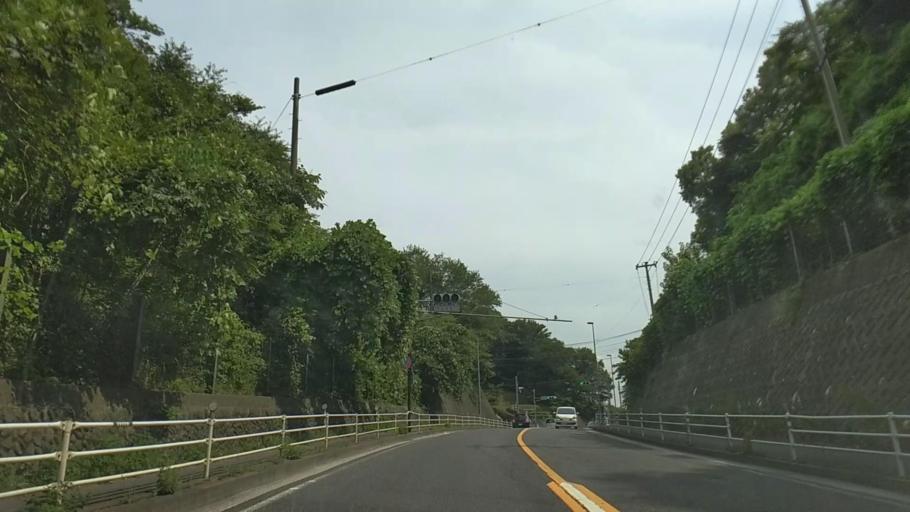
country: JP
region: Tokyo
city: Hachioji
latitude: 35.6220
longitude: 139.3410
